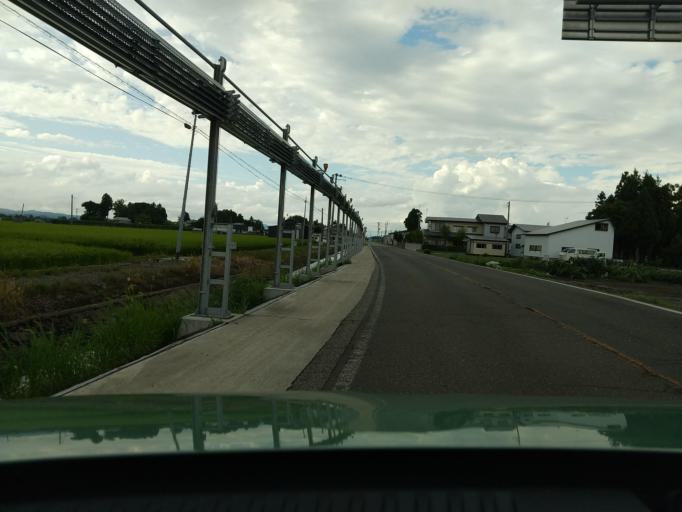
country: JP
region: Akita
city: Yokotemachi
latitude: 39.3170
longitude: 140.4901
